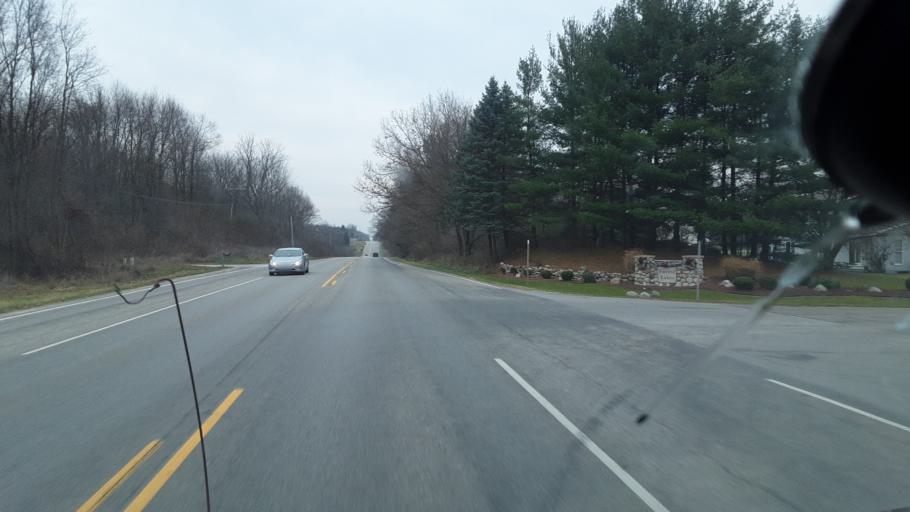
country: US
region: Indiana
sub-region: Elkhart County
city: Middlebury
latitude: 41.7259
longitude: -85.6650
